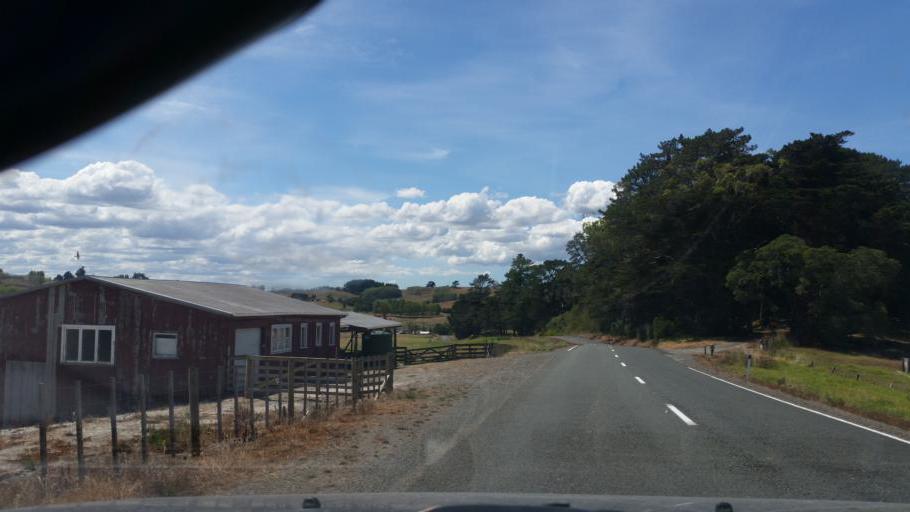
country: NZ
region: Northland
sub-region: Kaipara District
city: Dargaville
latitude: -36.1495
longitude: 174.1674
